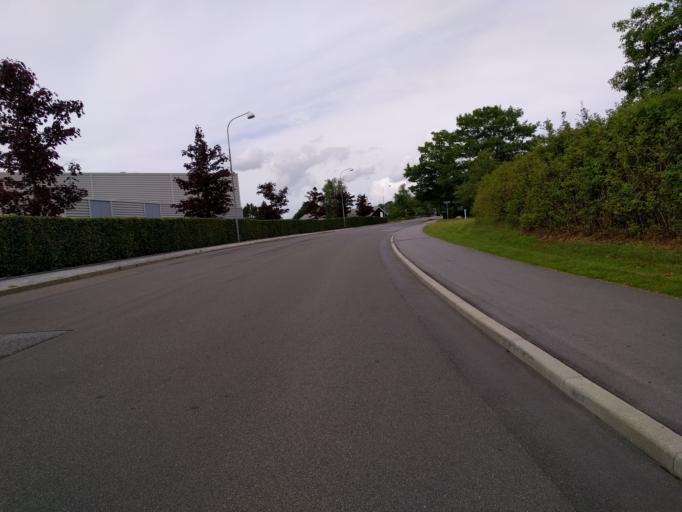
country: DK
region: Central Jutland
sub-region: Skanderborg Kommune
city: Ry
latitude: 56.0866
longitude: 9.7643
